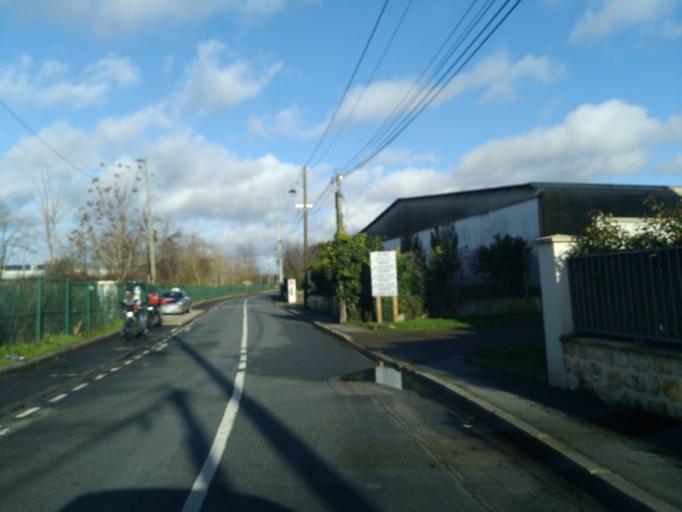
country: FR
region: Ile-de-France
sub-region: Departement des Yvelines
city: Villiers-Saint-Frederic
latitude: 48.8160
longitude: 1.8790
